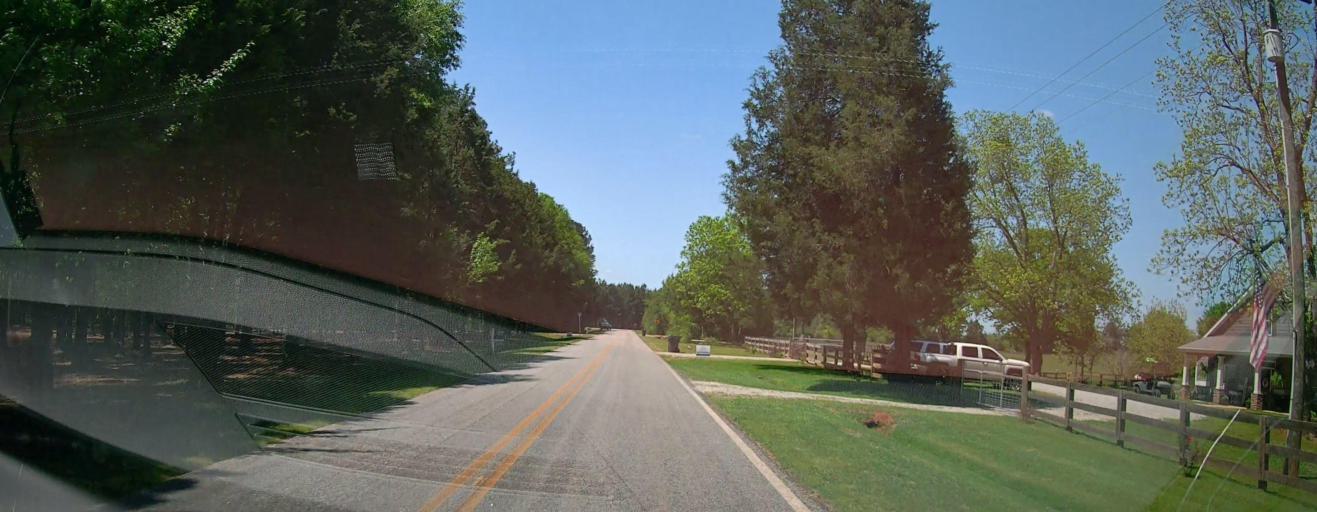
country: US
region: Georgia
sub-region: Jasper County
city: Monticello
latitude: 33.2797
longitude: -83.6704
